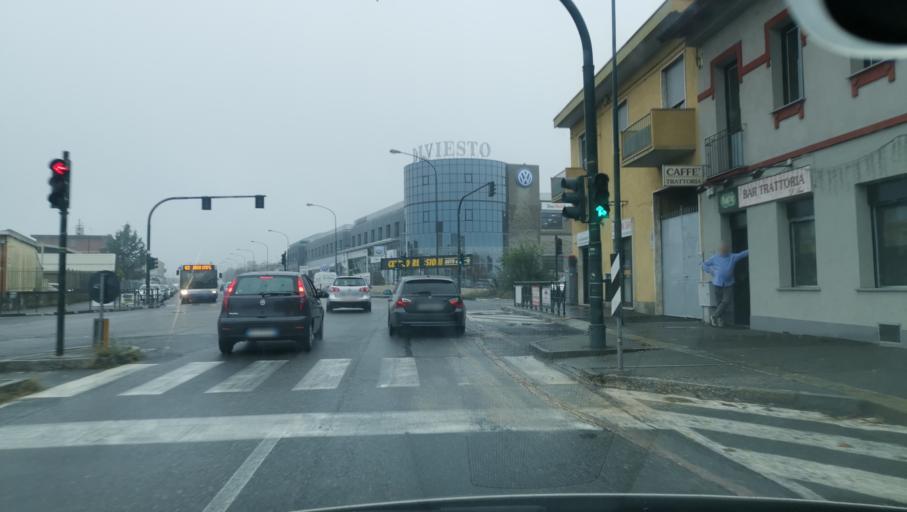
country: IT
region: Piedmont
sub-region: Provincia di Torino
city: Turin
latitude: 45.1095
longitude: 7.6859
